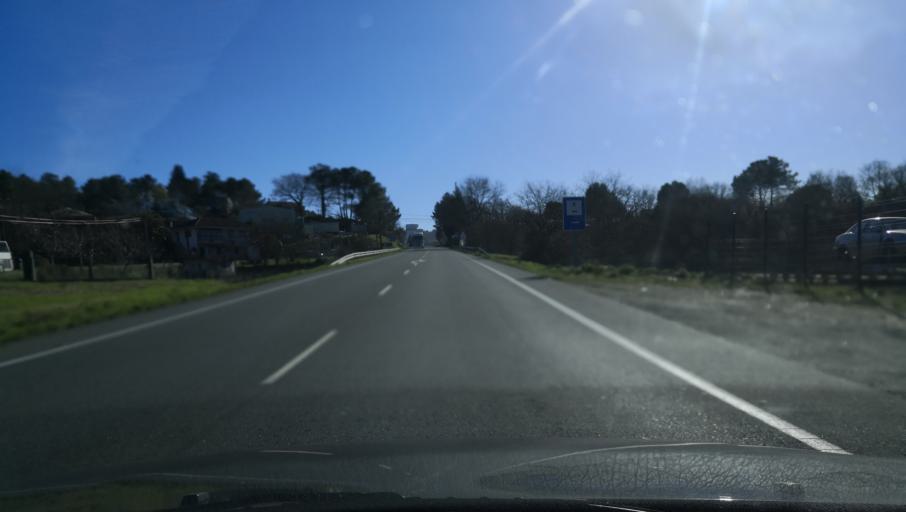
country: ES
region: Galicia
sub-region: Provincia de Pontevedra
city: Silleda
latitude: 42.7110
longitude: -8.2754
